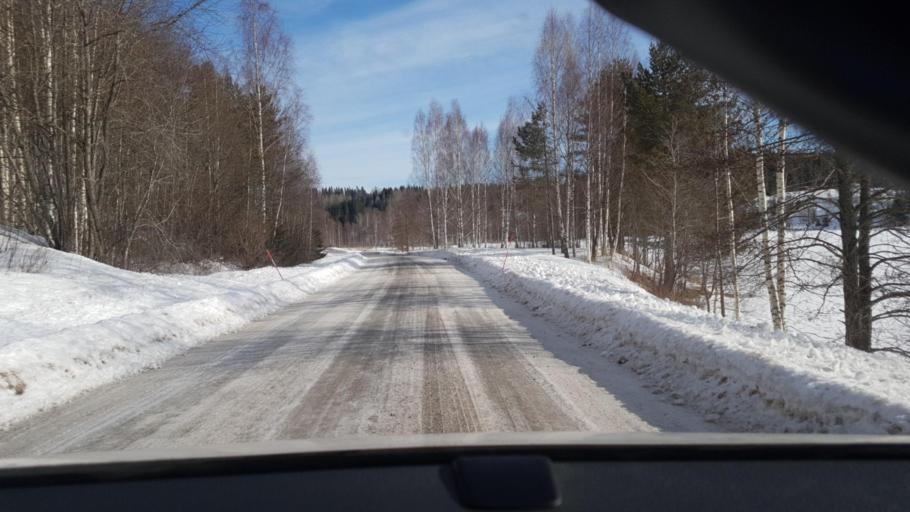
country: NO
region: Hedmark
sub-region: Eidskog
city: Skotterud
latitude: 59.8863
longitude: 11.9802
